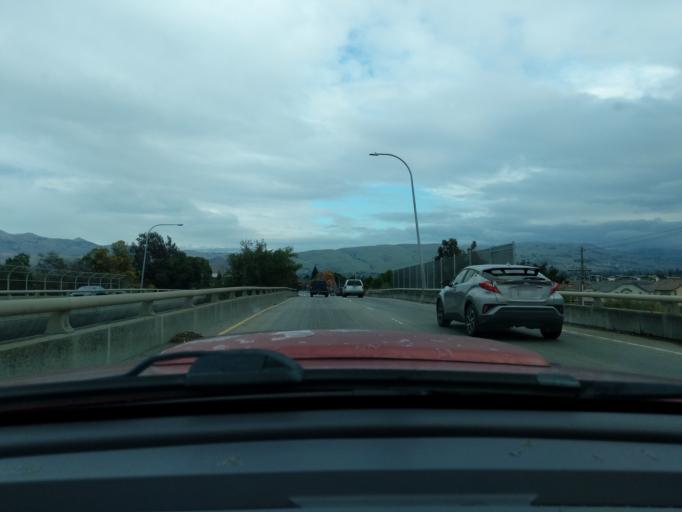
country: US
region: California
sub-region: Santa Clara County
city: Milpitas
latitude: 37.4318
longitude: -121.9035
